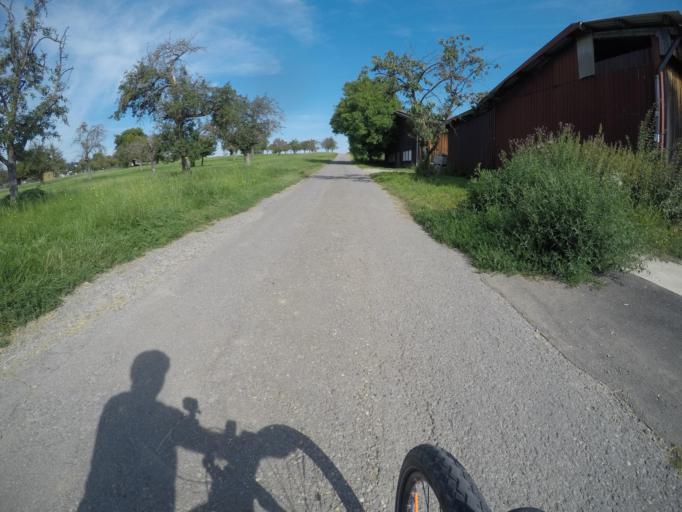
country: DE
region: Baden-Wuerttemberg
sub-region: Karlsruhe Region
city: Wiernsheim
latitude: 48.8935
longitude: 8.8563
